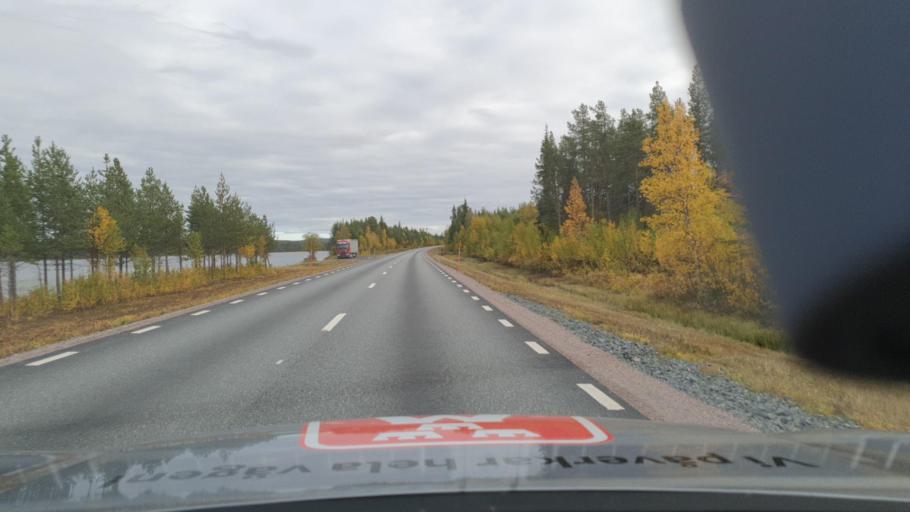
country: SE
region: Norrbotten
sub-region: Arjeplogs Kommun
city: Arjeplog
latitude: 65.9764
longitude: 18.2373
